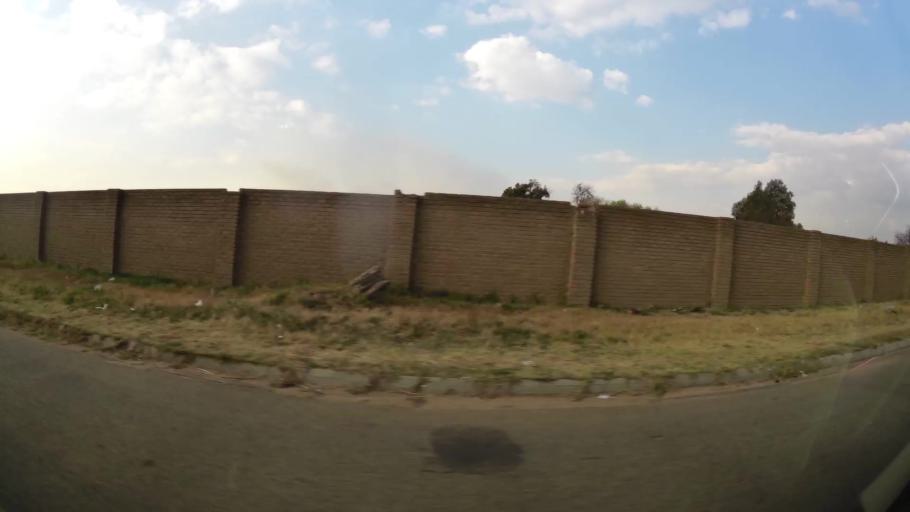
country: ZA
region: Gauteng
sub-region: Ekurhuleni Metropolitan Municipality
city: Benoni
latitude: -26.1414
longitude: 28.2958
